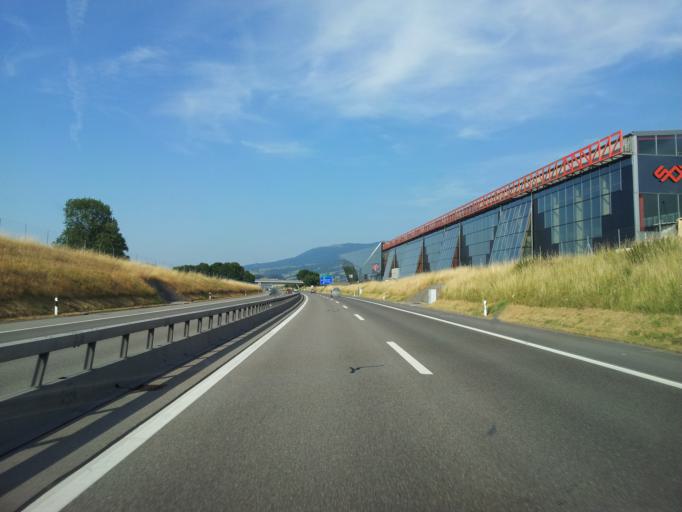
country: CH
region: Fribourg
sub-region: Gruyere District
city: Vuadens
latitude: 46.6256
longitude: 7.0354
